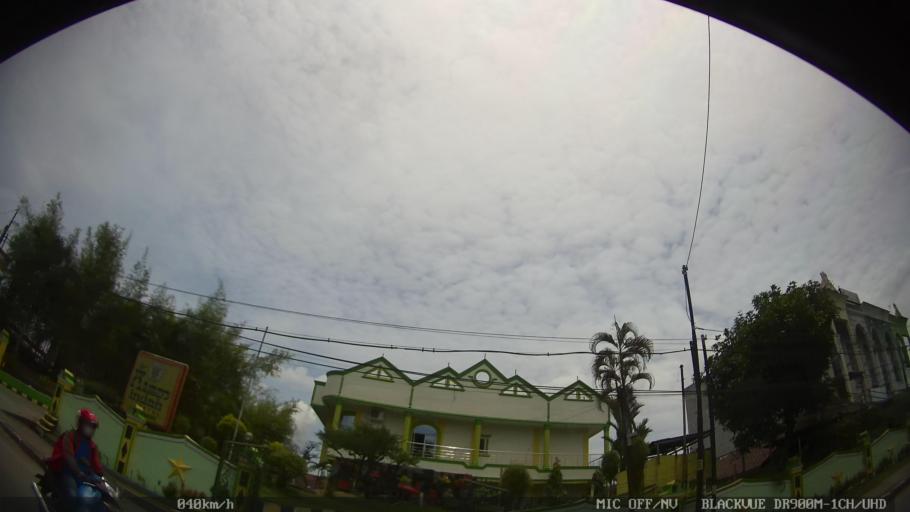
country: ID
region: North Sumatra
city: Deli Tua
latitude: 3.5318
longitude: 98.6435
